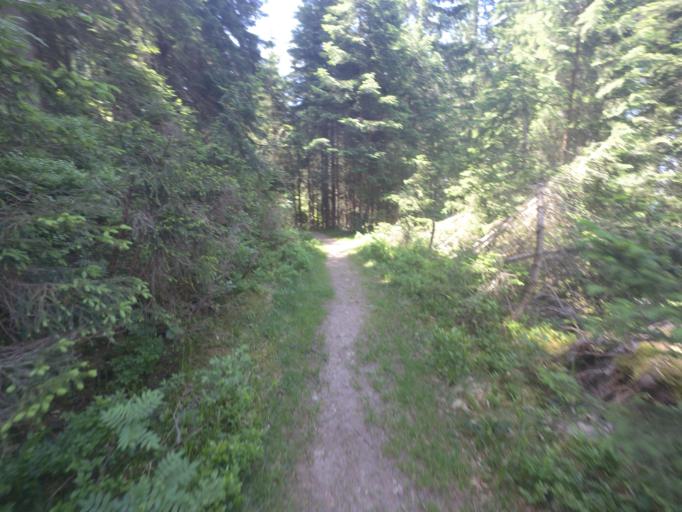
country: AT
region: Salzburg
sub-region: Politischer Bezirk Zell am See
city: Dienten am Hochkonig
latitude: 47.4153
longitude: 13.0008
